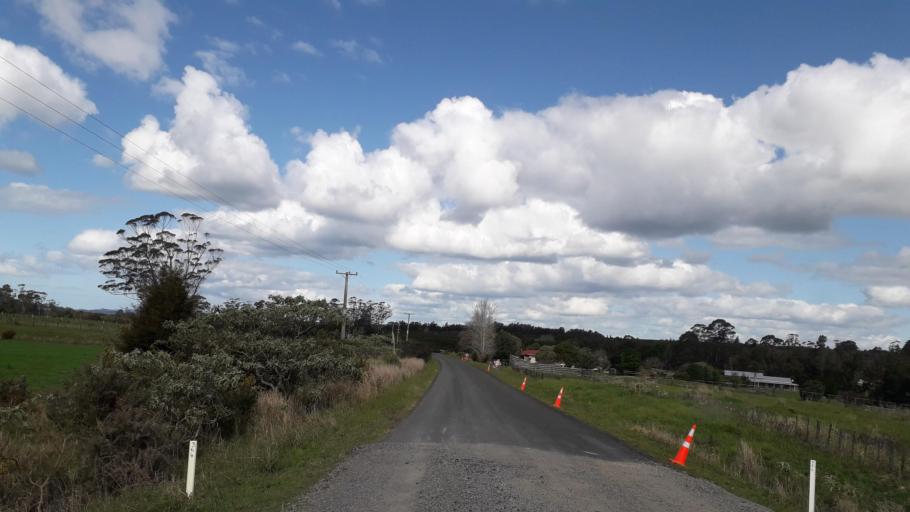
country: NZ
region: Northland
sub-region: Far North District
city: Kerikeri
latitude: -35.1842
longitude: 173.9377
